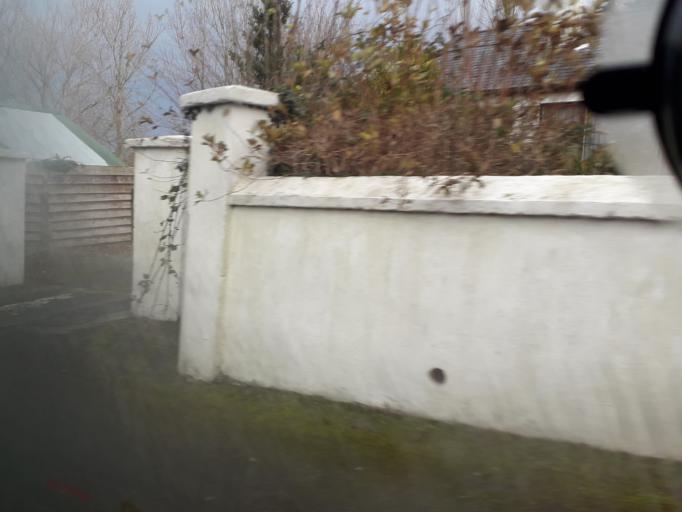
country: IE
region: Leinster
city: Ballyboden
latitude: 53.2486
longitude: -6.2993
